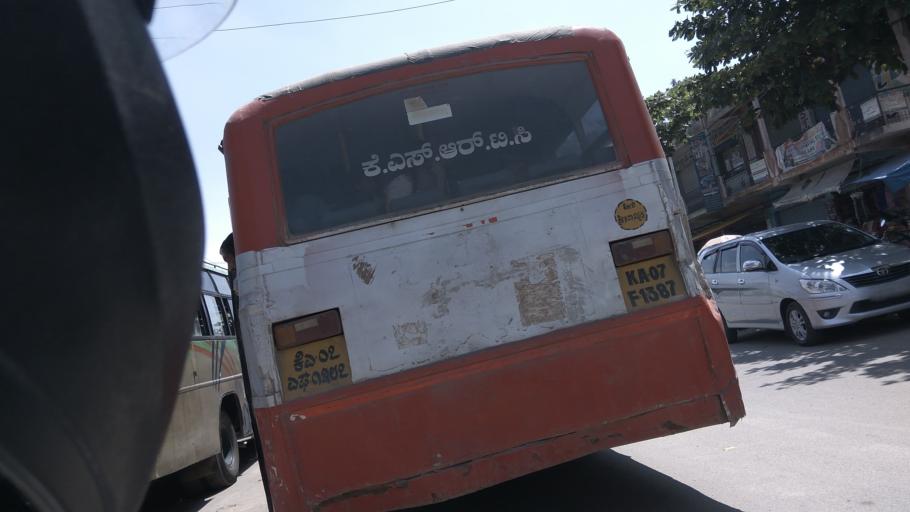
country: IN
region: Karnataka
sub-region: Kolar
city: Mulbagal
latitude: 13.1655
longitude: 78.3944
